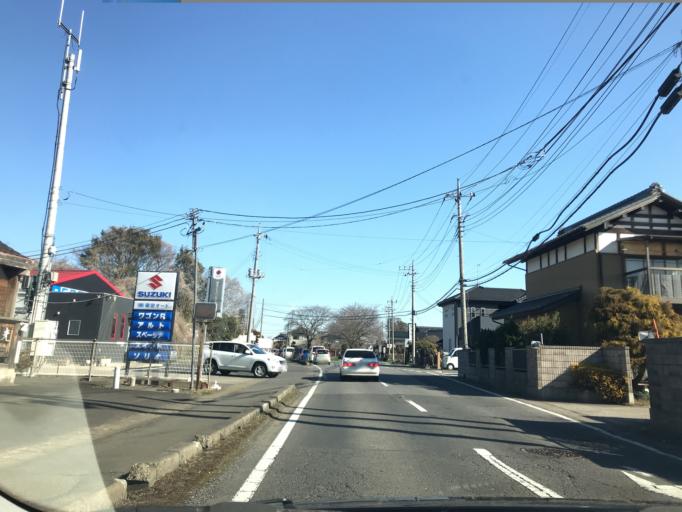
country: JP
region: Ibaraki
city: Ishige
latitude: 36.1026
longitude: 140.0482
